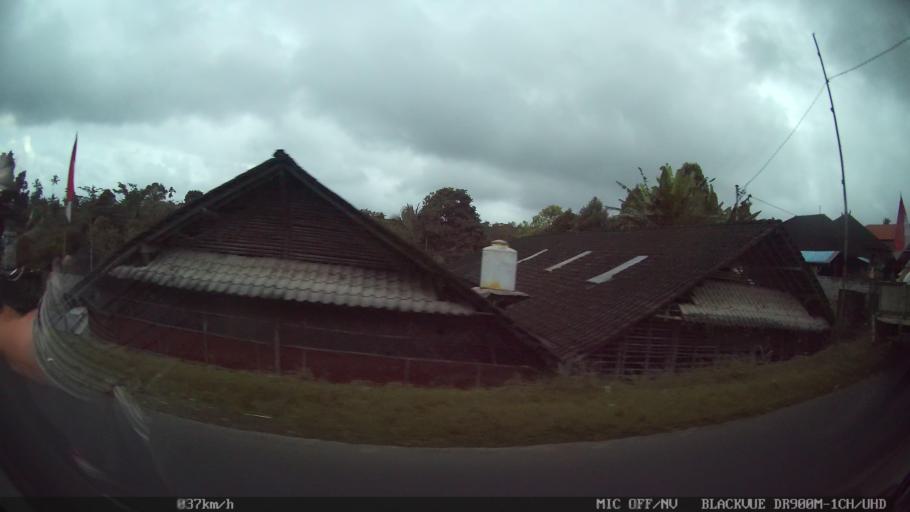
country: ID
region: Bali
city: Empalan
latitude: -8.3871
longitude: 115.1509
